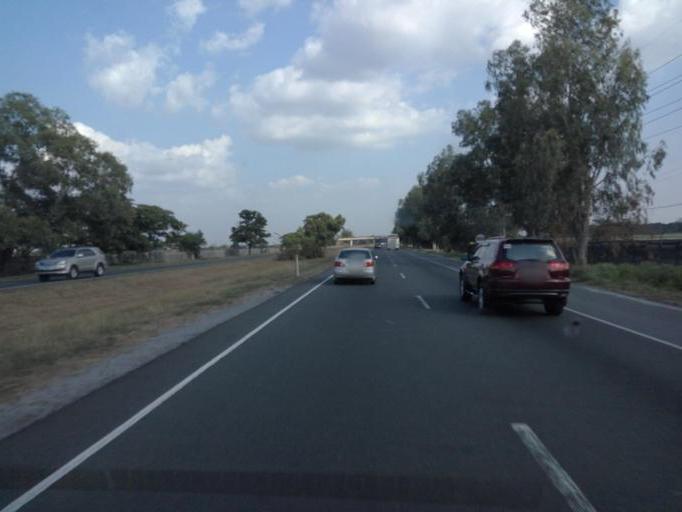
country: PH
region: Central Luzon
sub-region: Province of Pampanga
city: Acli
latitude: 15.1352
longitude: 120.6382
